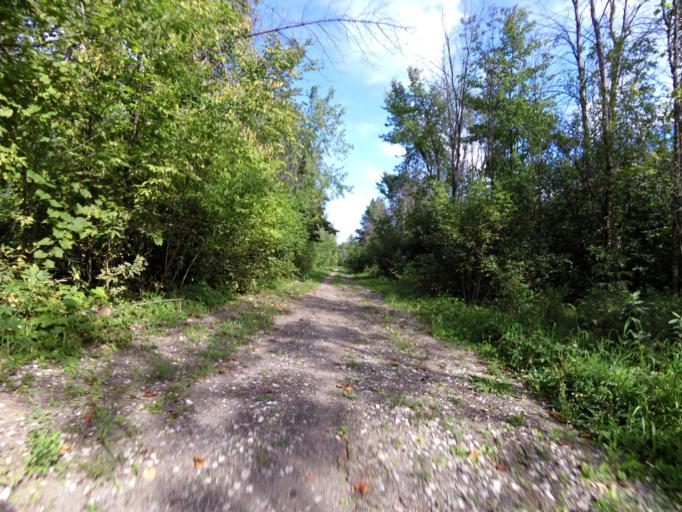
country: CA
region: Quebec
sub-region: Outaouais
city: Gatineau
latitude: 45.5014
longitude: -75.7809
